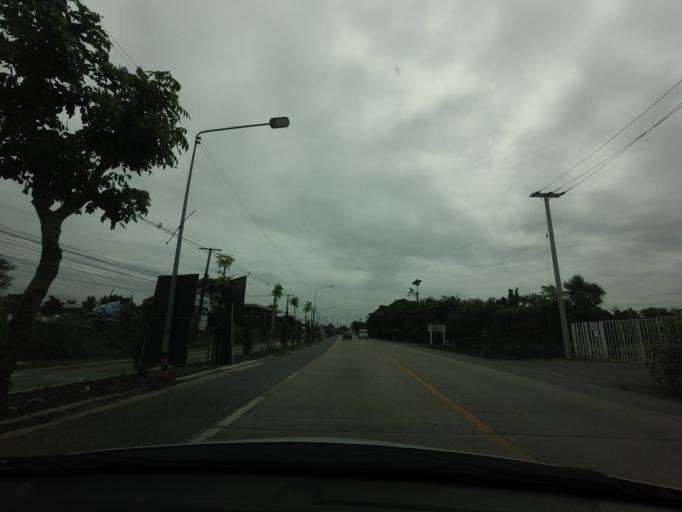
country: TH
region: Pathum Thani
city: Lam Luk Ka
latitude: 13.9295
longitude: 100.7286
